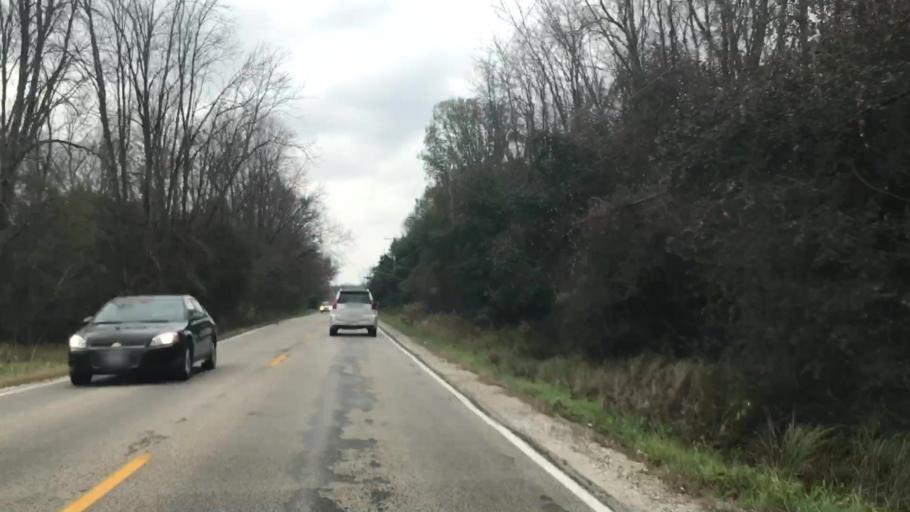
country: US
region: Wisconsin
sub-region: Waukesha County
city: Menomonee Falls
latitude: 43.2027
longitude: -88.1427
